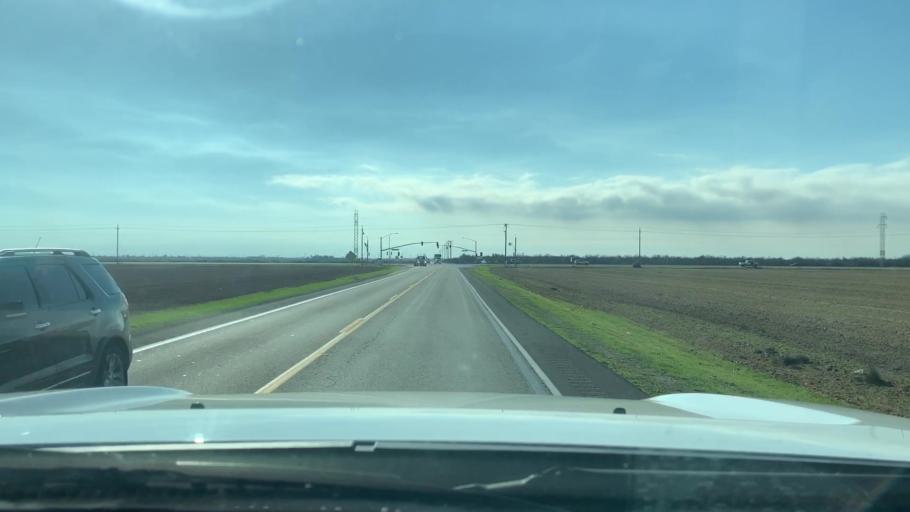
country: US
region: California
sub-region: Kern County
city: Rosedale
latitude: 35.4441
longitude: -119.1543
